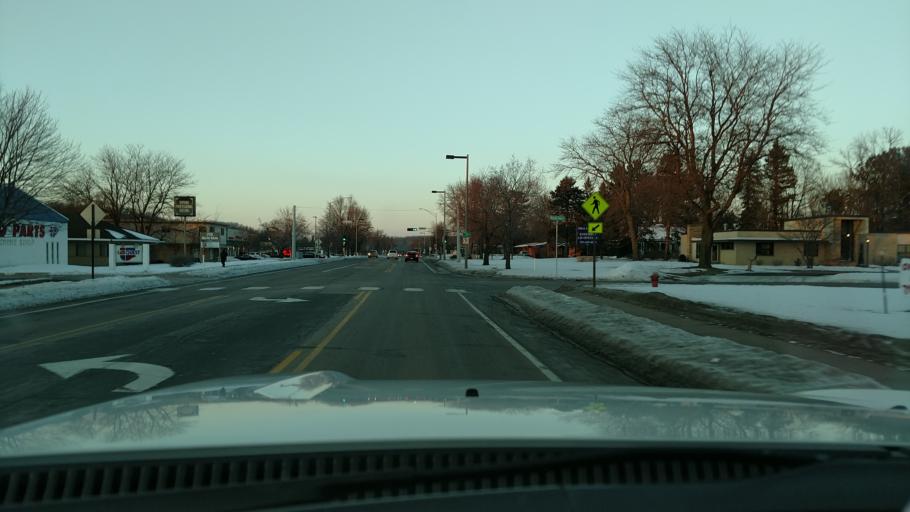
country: US
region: Wisconsin
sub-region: Pierce County
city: River Falls
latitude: 44.8686
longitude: -92.6218
